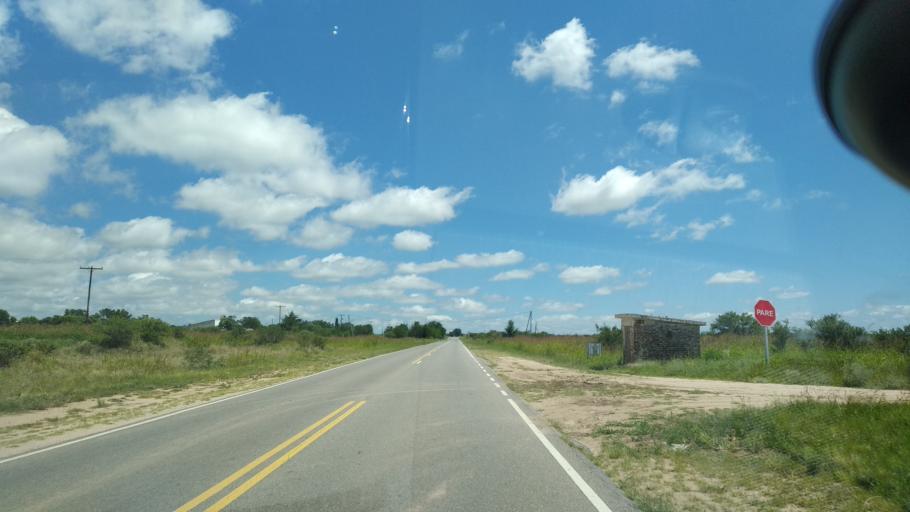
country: AR
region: Cordoba
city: Villa Cura Brochero
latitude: -31.6280
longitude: -65.1069
